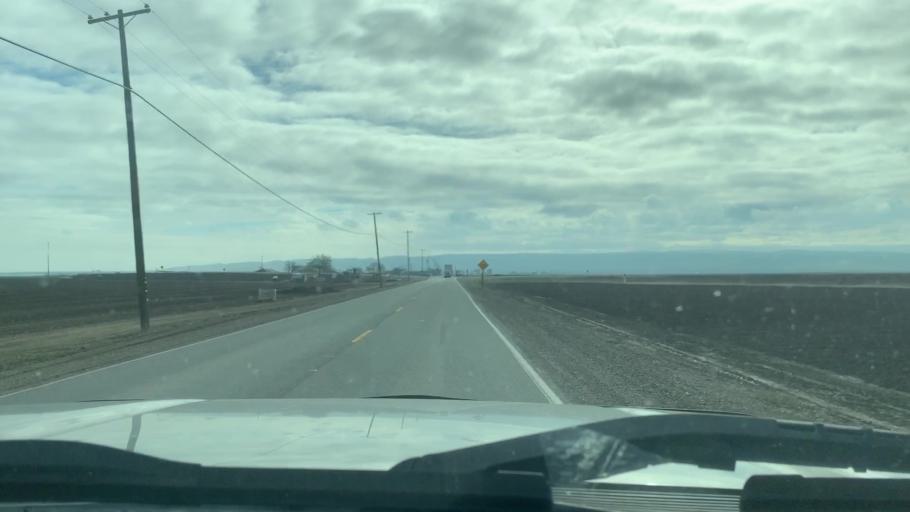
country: US
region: California
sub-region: Merced County
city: Los Banos
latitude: 36.9804
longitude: -120.8374
